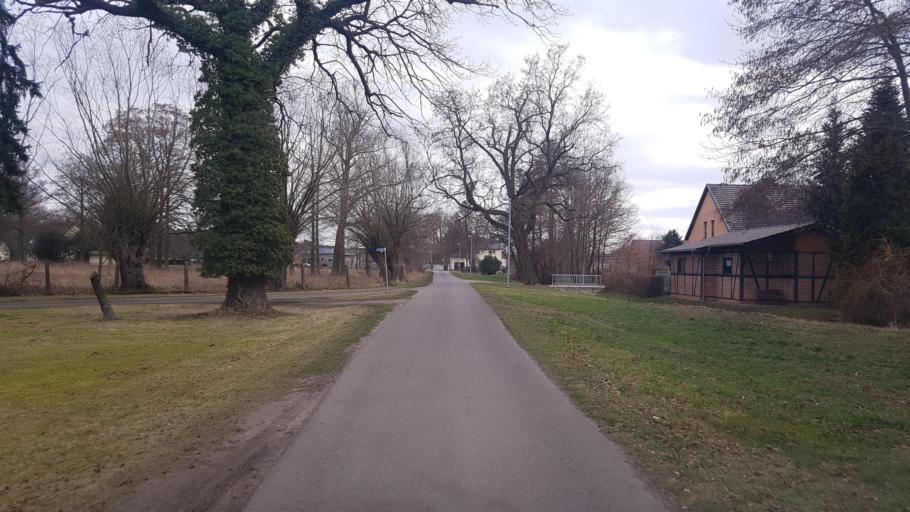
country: DE
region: Brandenburg
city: Golssen
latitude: 51.9431
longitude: 13.6215
